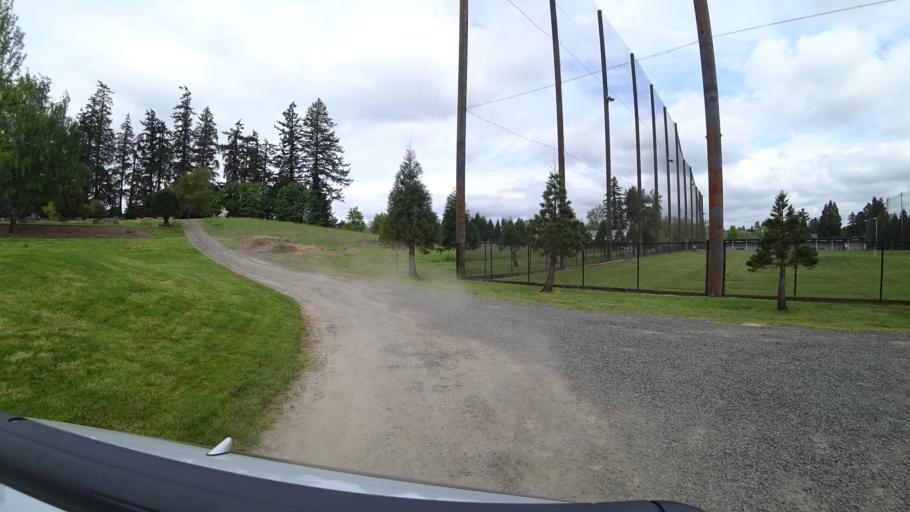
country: US
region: Oregon
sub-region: Washington County
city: Hillsboro
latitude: 45.5233
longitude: -123.0043
